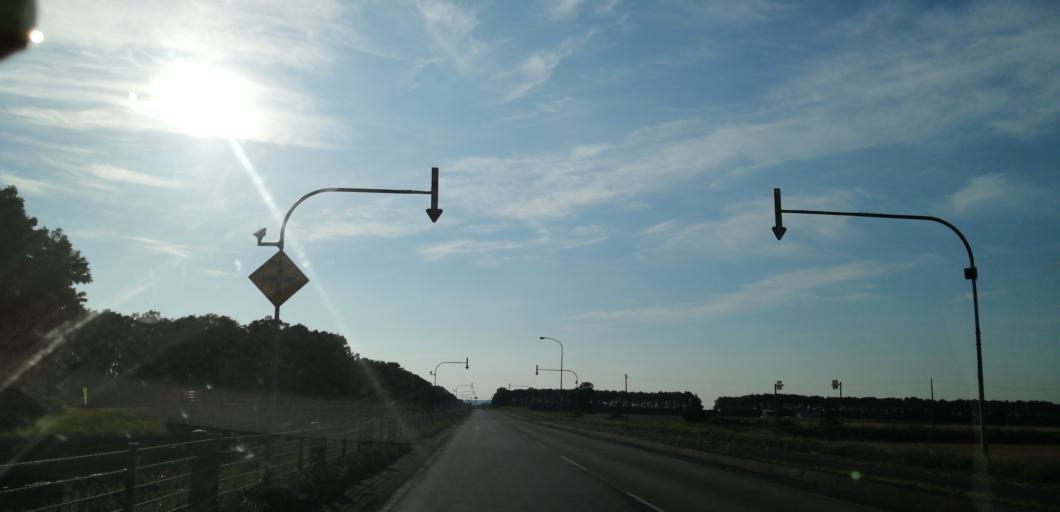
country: JP
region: Hokkaido
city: Kitahiroshima
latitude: 42.9757
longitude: 141.6479
